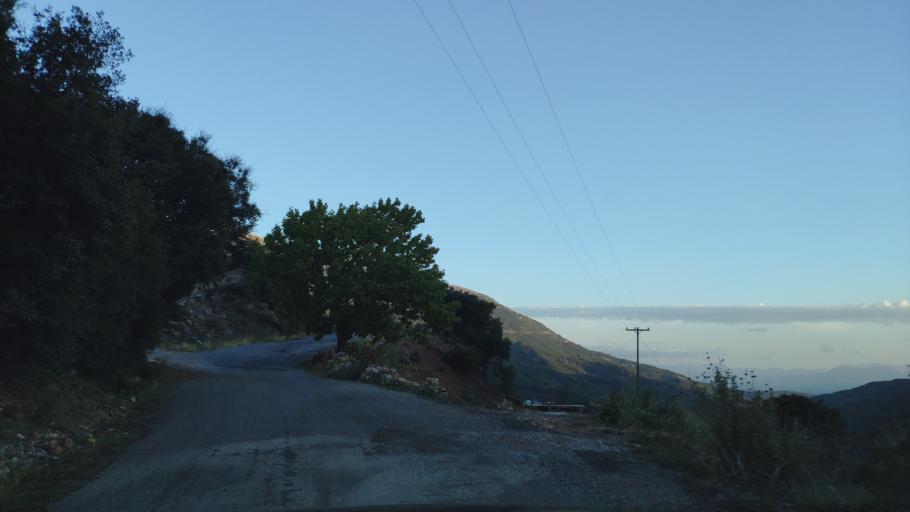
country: GR
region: Peloponnese
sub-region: Nomos Arkadias
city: Dimitsana
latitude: 37.5876
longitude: 22.0380
